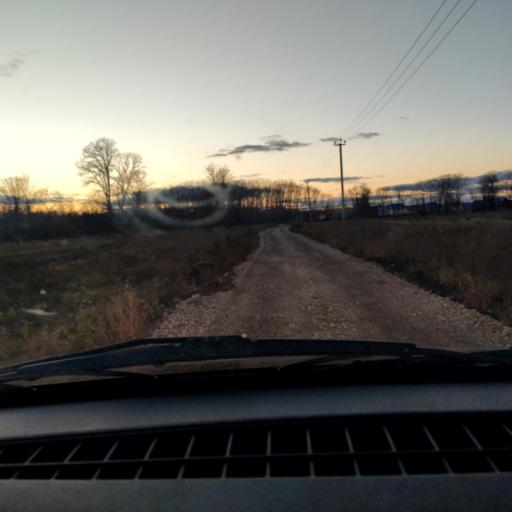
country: RU
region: Bashkortostan
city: Ufa
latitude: 54.6467
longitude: 55.9041
